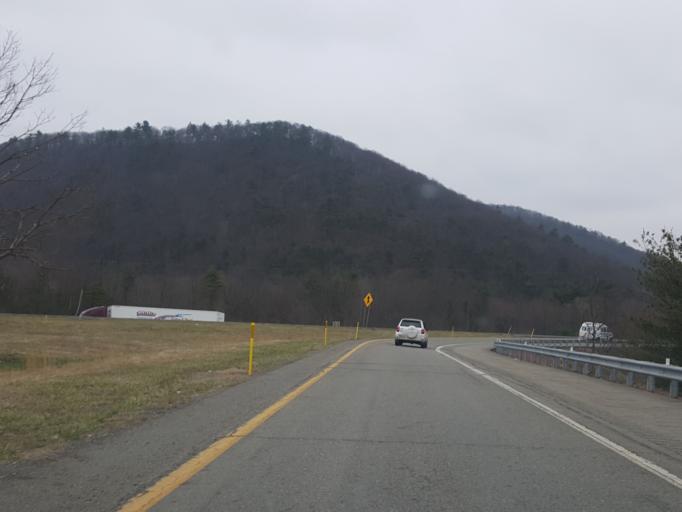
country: US
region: Pennsylvania
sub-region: Schuylkill County
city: Tremont
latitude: 40.5901
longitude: -76.4138
